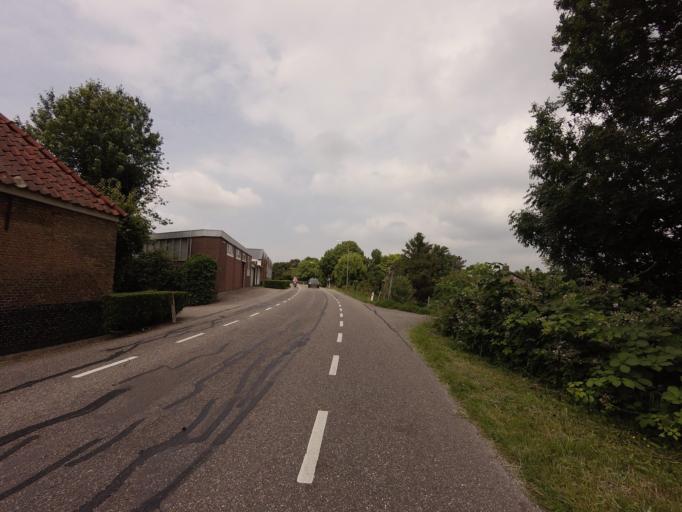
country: NL
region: South Holland
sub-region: Gemeente Krimpen aan den IJssel
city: Krimpen aan den IJssel
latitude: 51.9421
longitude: 4.6384
